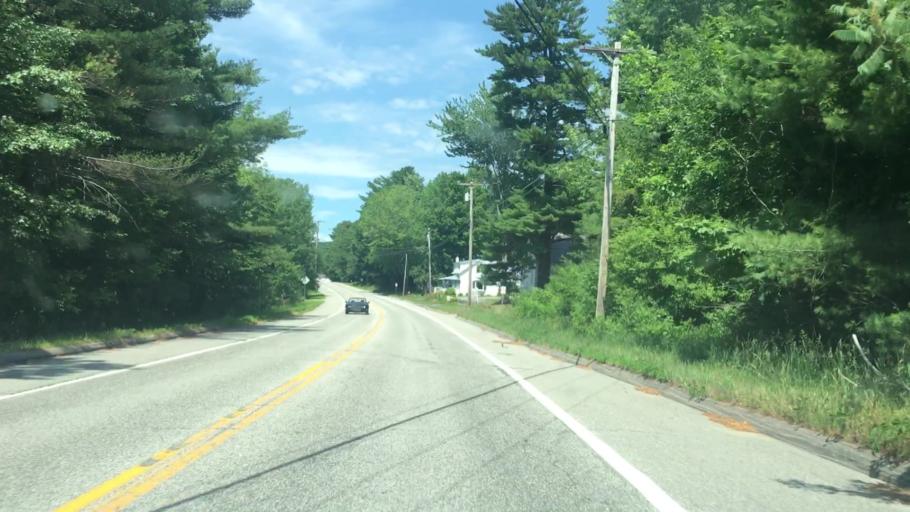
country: US
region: Maine
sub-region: Kennebec County
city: Wayne
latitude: 44.3521
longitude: -70.0727
